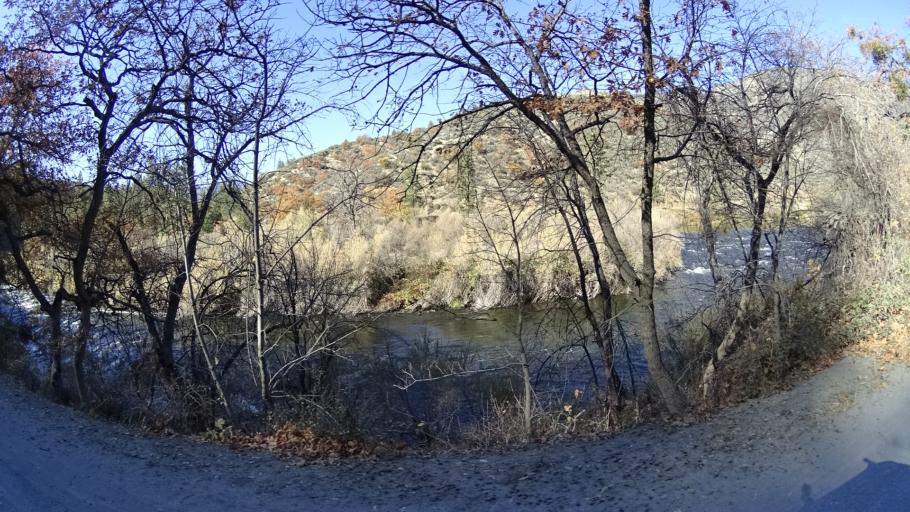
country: US
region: California
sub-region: Siskiyou County
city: Yreka
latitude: 41.8287
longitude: -122.6407
